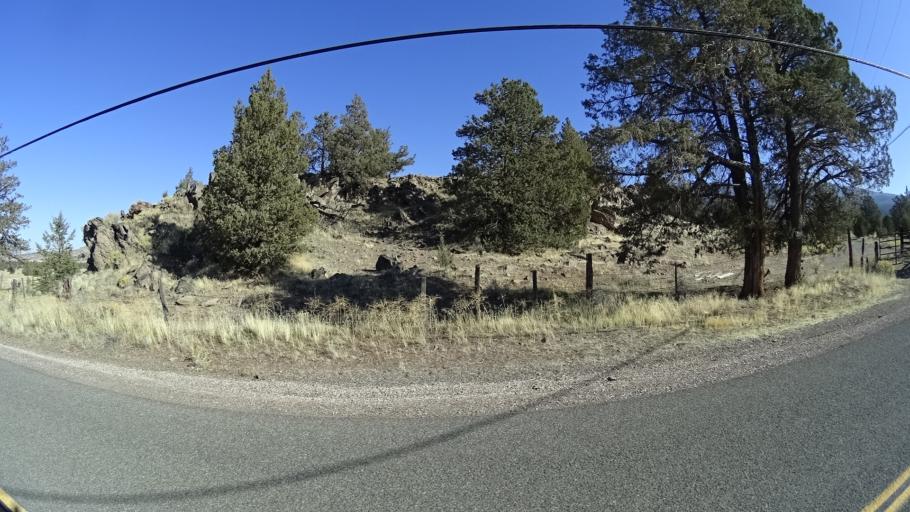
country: US
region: California
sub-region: Siskiyou County
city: Montague
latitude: 41.6399
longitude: -122.3420
